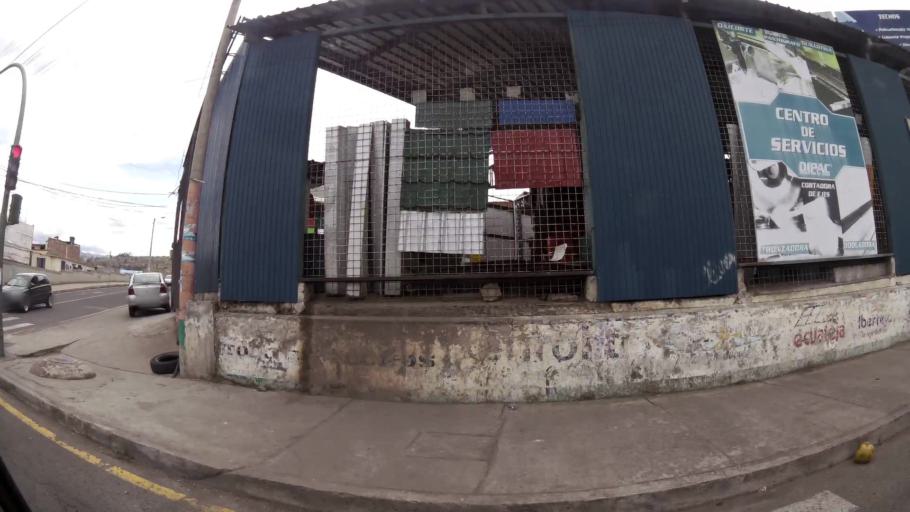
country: EC
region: Tungurahua
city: Ambato
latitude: -1.2788
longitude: -78.6306
